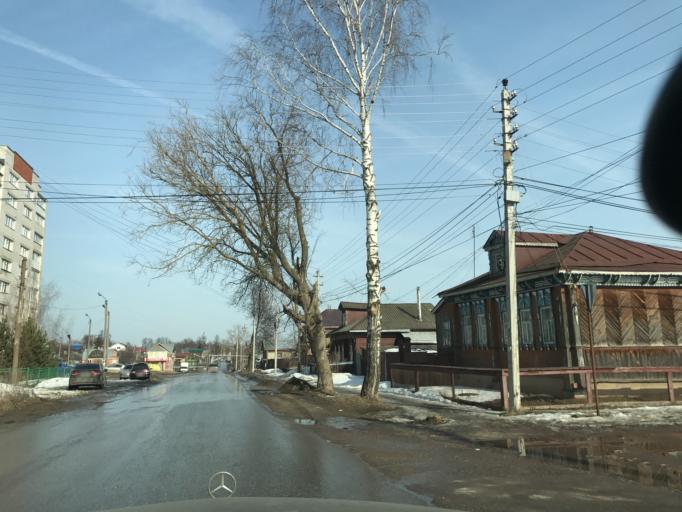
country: RU
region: Nizjnij Novgorod
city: Taremskoye
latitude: 55.9548
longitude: 43.0513
